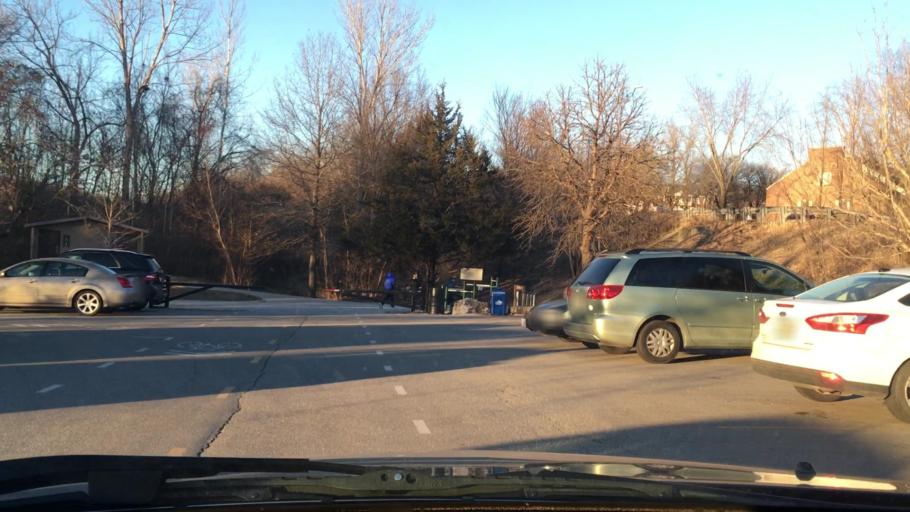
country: US
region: Missouri
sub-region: Boone County
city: Columbia
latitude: 38.9231
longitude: -92.3658
